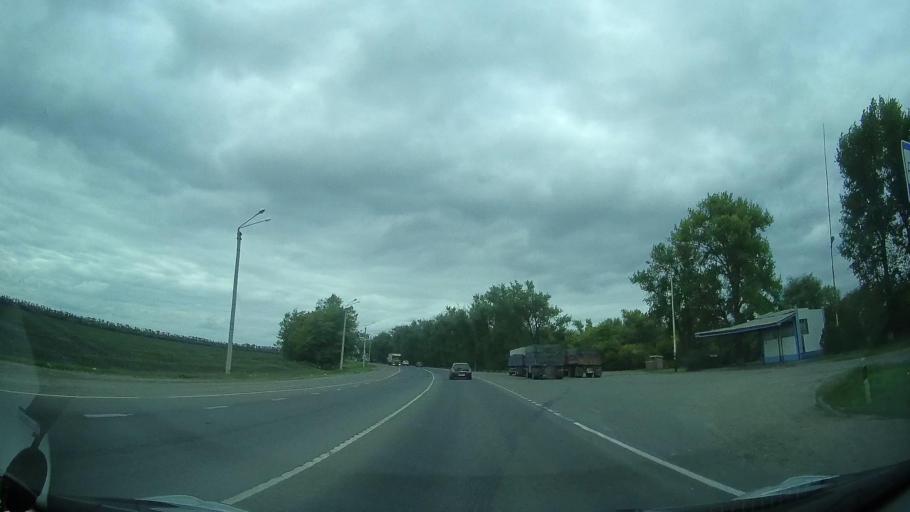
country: RU
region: Rostov
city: Yegorlykskaya
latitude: 46.5875
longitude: 40.6316
